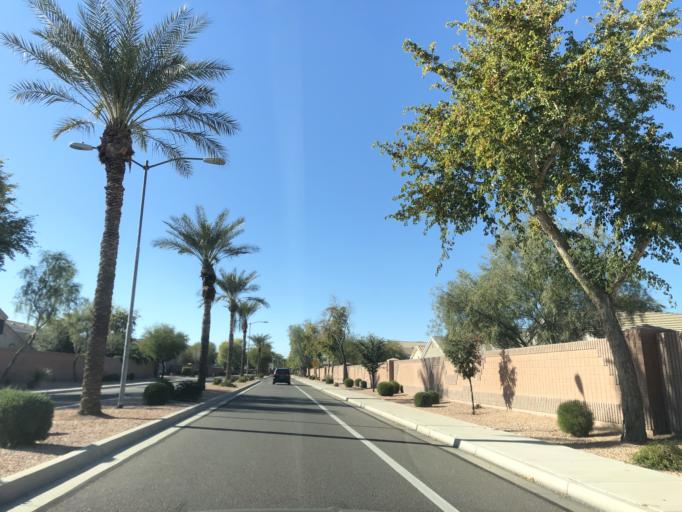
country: US
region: Arizona
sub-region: Maricopa County
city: El Mirage
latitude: 33.6161
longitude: -112.3369
